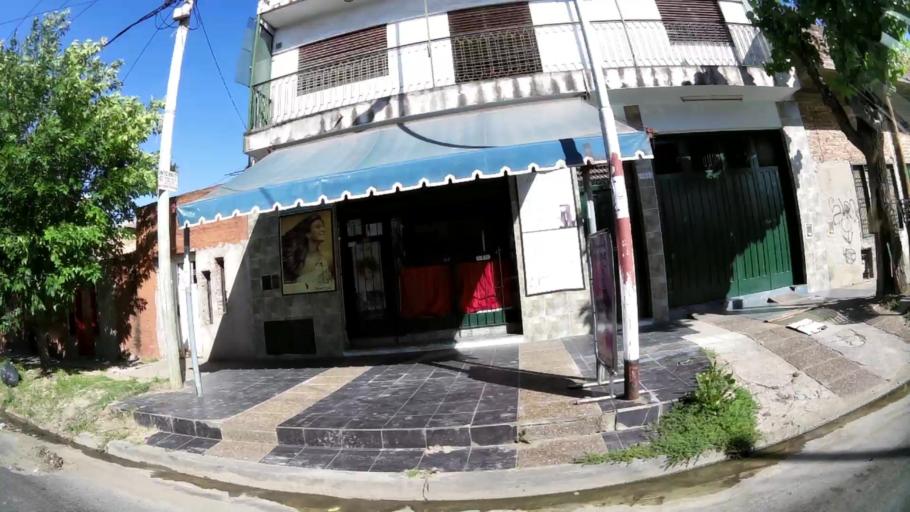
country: AR
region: Buenos Aires
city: Hurlingham
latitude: -34.5557
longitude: -58.6080
